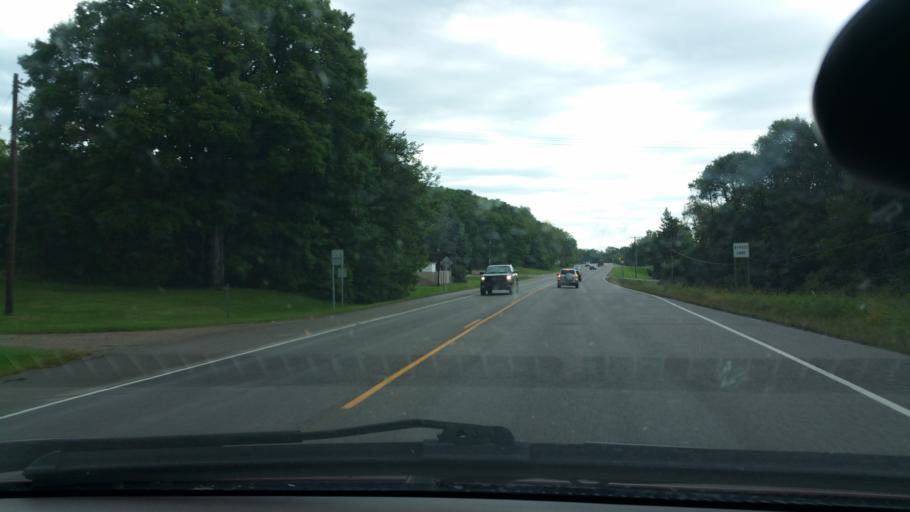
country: US
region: Minnesota
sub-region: Rice County
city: Northfield
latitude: 44.4569
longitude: -93.1903
